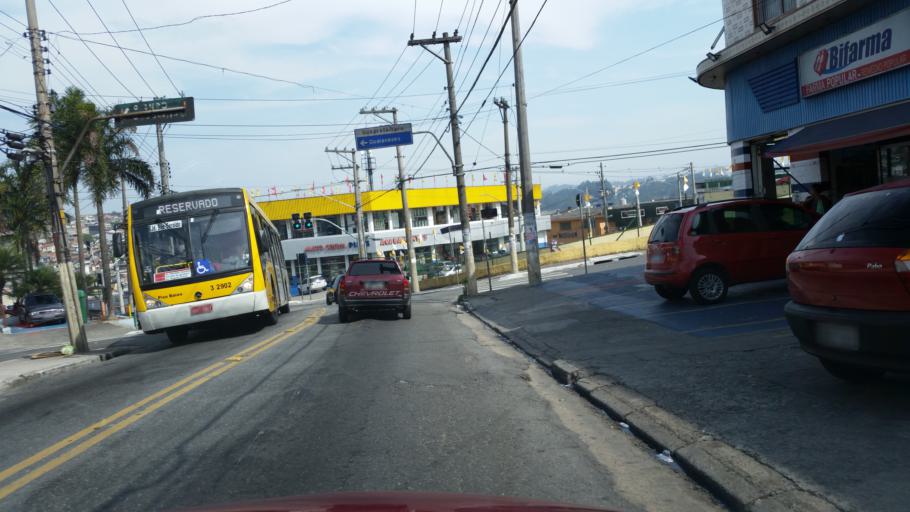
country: BR
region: Sao Paulo
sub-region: Ferraz De Vasconcelos
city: Ferraz de Vasconcelos
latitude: -23.5423
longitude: -46.4252
